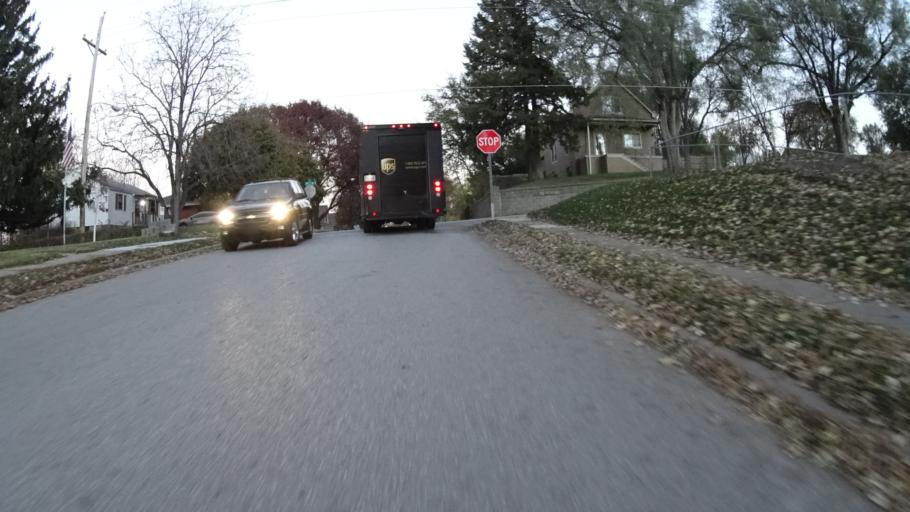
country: US
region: Nebraska
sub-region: Douglas County
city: Omaha
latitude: 41.1918
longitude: -95.9459
